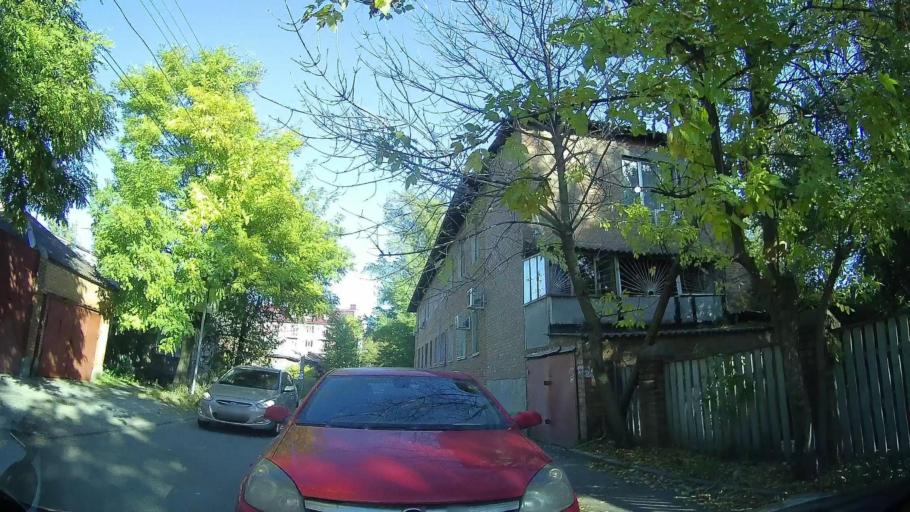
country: RU
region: Rostov
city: Rostov-na-Donu
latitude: 47.2122
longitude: 39.6853
